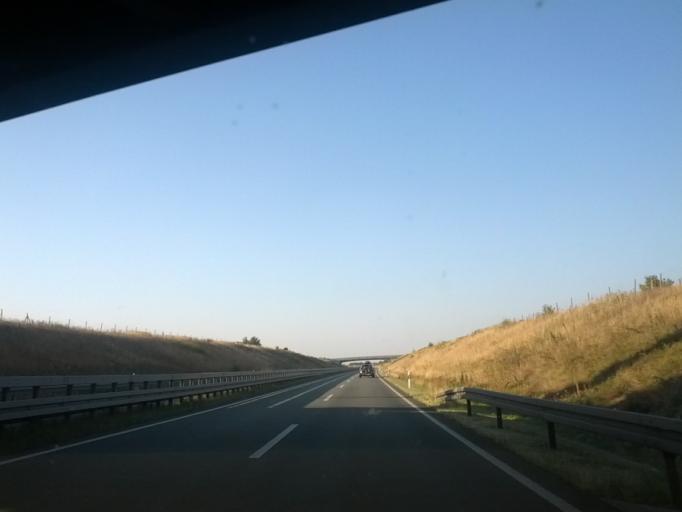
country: DE
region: Mecklenburg-Vorpommern
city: Brandshagen
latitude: 54.2213
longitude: 13.1535
